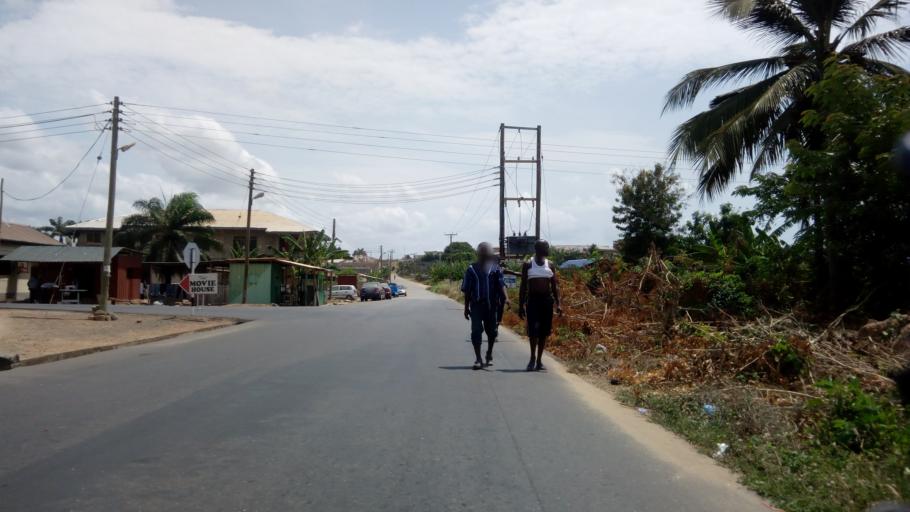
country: GH
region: Central
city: Cape Coast
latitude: 5.1237
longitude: -1.2762
